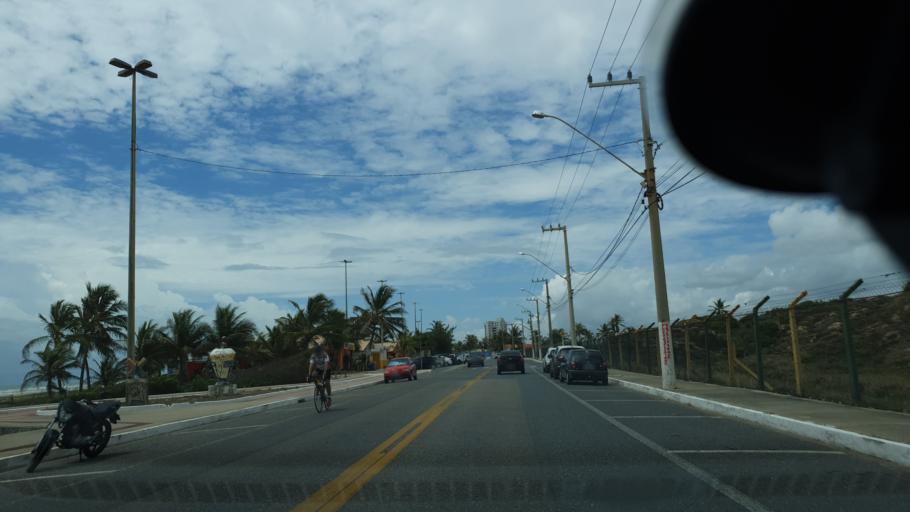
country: BR
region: Sergipe
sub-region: Aracaju
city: Aracaju
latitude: -11.0132
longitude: -37.0668
